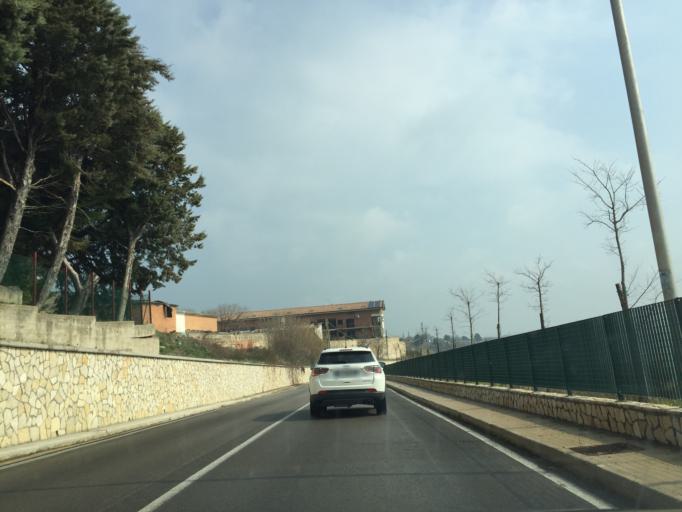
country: IT
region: Apulia
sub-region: Provincia di Foggia
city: Troia
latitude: 41.3653
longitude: 15.3223
